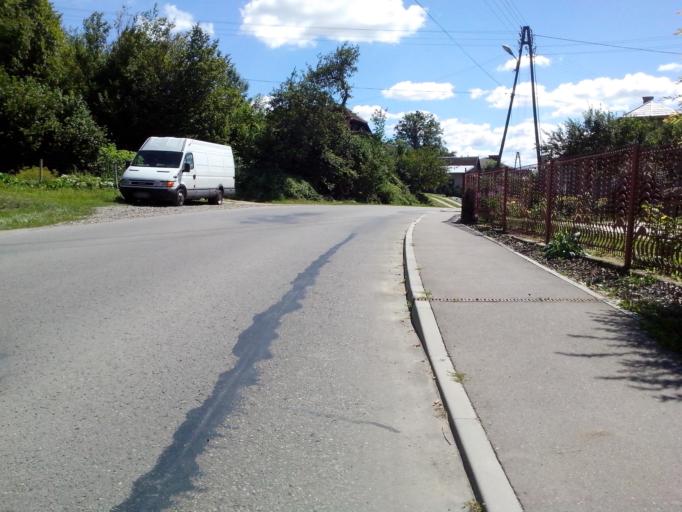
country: PL
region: Subcarpathian Voivodeship
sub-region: Powiat brzozowski
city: Domaradz
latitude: 49.7934
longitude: 21.9513
